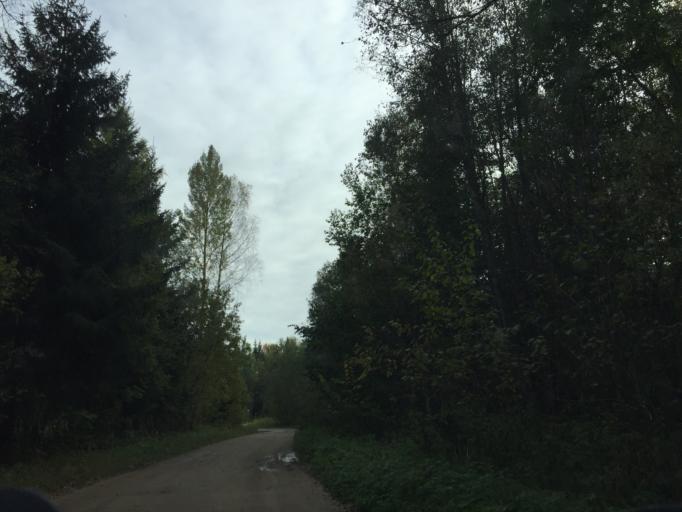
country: LV
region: Jaunpils
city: Jaunpils
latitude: 56.5698
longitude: 23.0290
